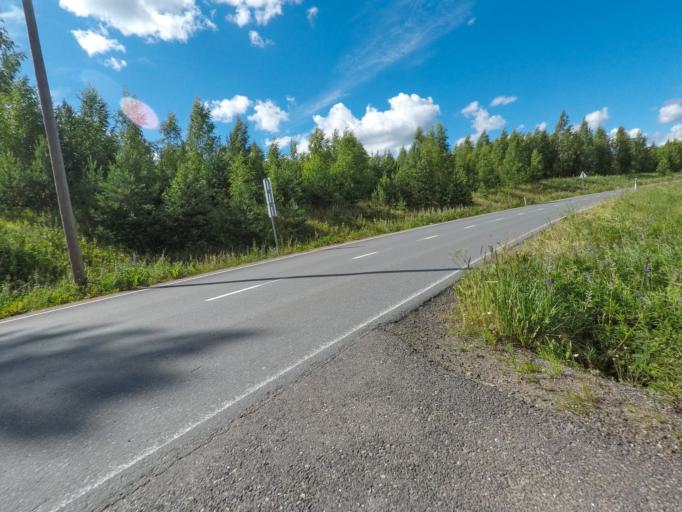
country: FI
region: South Karelia
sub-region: Lappeenranta
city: Joutseno
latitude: 61.0924
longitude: 28.3525
